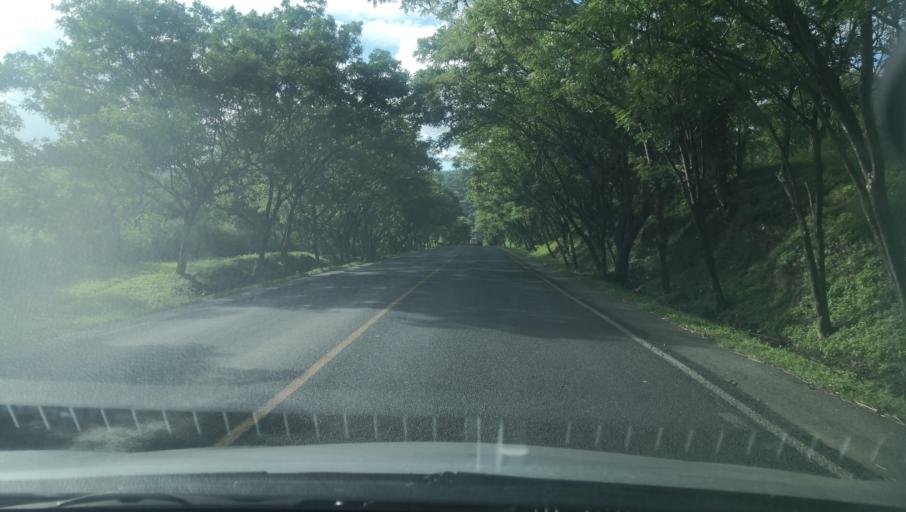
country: NI
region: Madriz
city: Totogalpa
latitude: 13.5796
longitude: -86.4771
